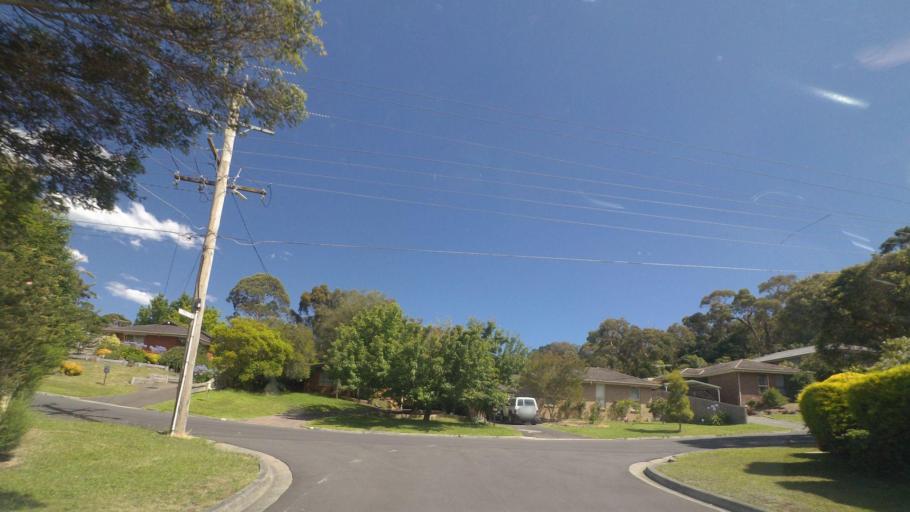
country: AU
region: Victoria
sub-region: Yarra Ranges
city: Montrose
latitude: -37.8050
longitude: 145.3366
